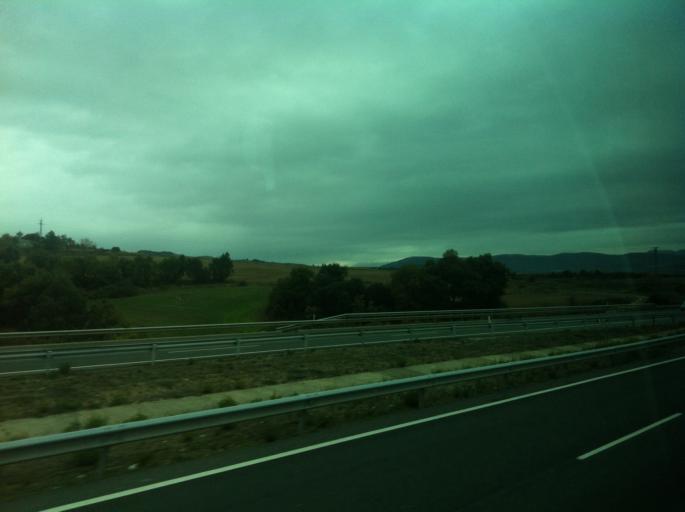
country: ES
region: Basque Country
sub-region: Provincia de Alava
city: Arminon
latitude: 42.7791
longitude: -2.8239
